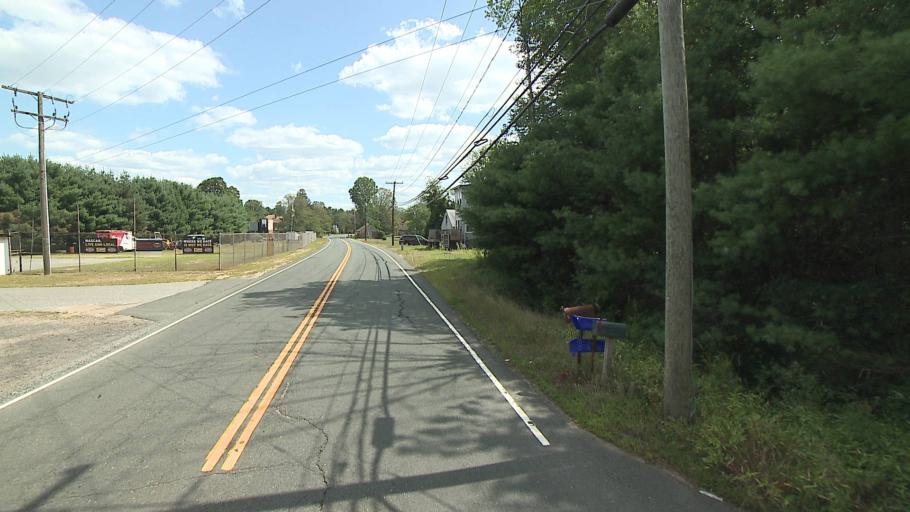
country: US
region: Connecticut
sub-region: Tolland County
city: Stafford Springs
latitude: 41.9537
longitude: -72.3208
